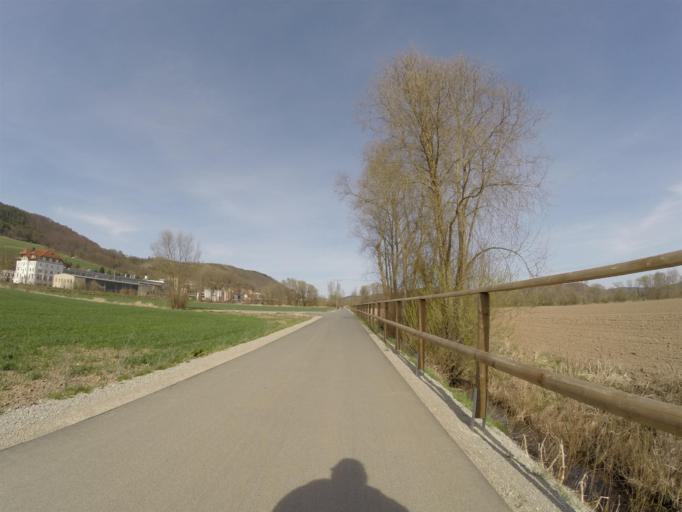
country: DE
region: Thuringia
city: Neuengonna
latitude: 50.9717
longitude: 11.6400
